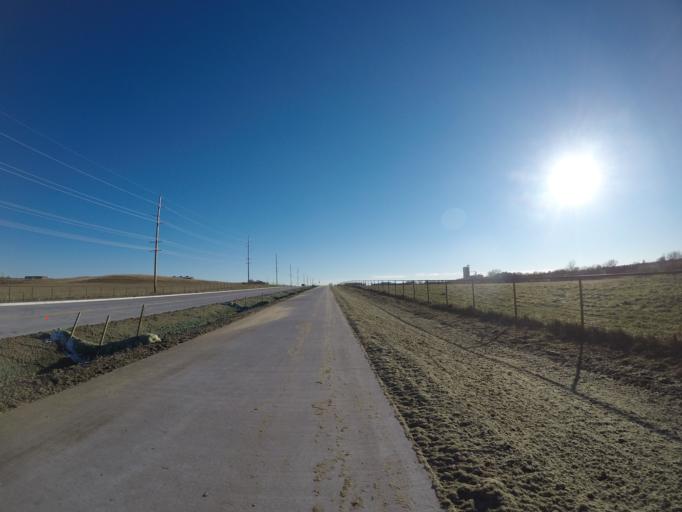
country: US
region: Kansas
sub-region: Riley County
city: Manhattan
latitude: 39.2131
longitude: -96.5858
